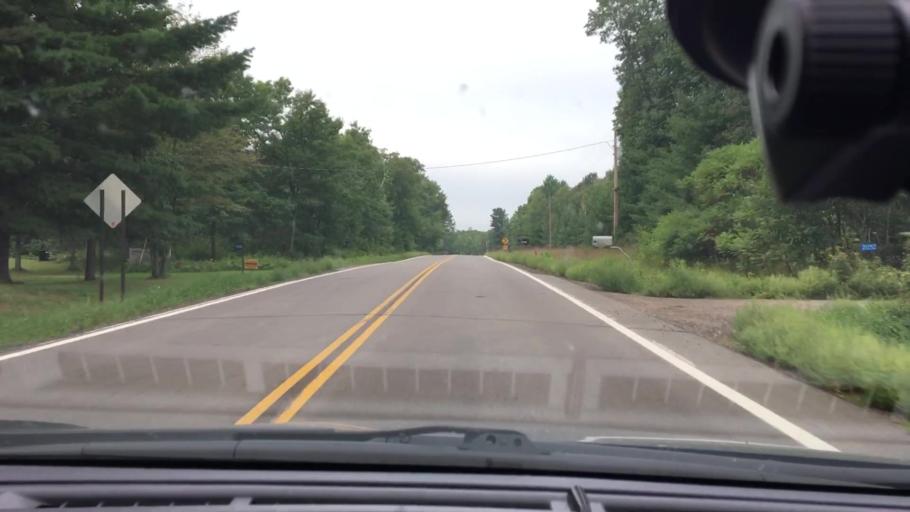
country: US
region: Minnesota
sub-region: Crow Wing County
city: Cross Lake
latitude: 46.6622
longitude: -93.9570
